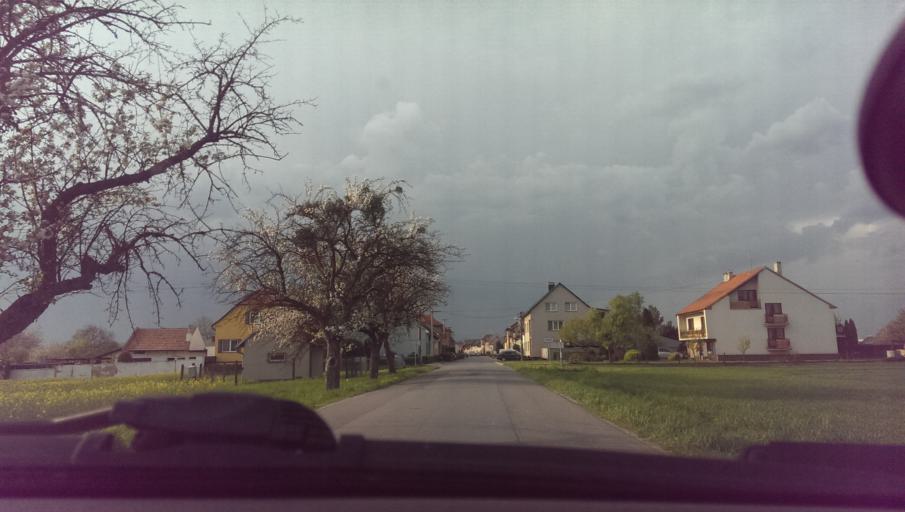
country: CZ
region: Zlin
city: Knezpole
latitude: 49.0944
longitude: 17.5193
